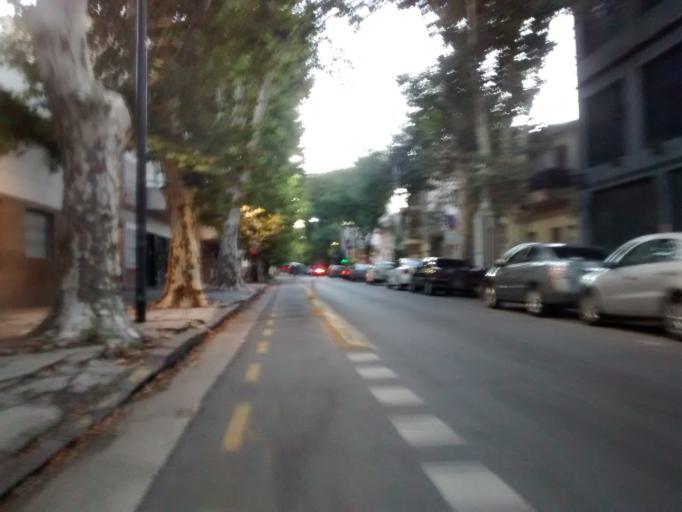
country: AR
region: Buenos Aires F.D.
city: Villa Santa Rita
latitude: -34.6072
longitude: -58.4569
